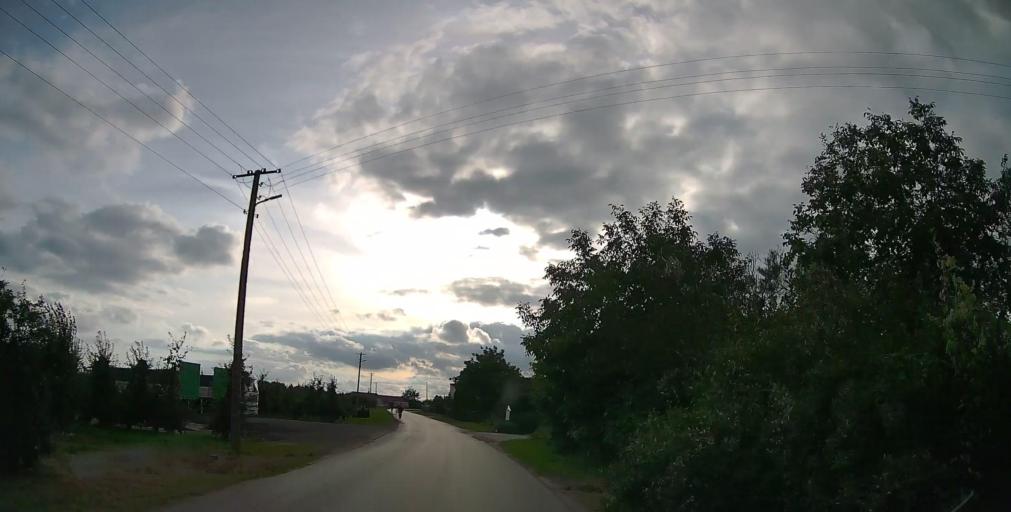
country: PL
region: Masovian Voivodeship
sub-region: Powiat grojecki
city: Jasieniec
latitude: 51.7569
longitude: 20.9227
